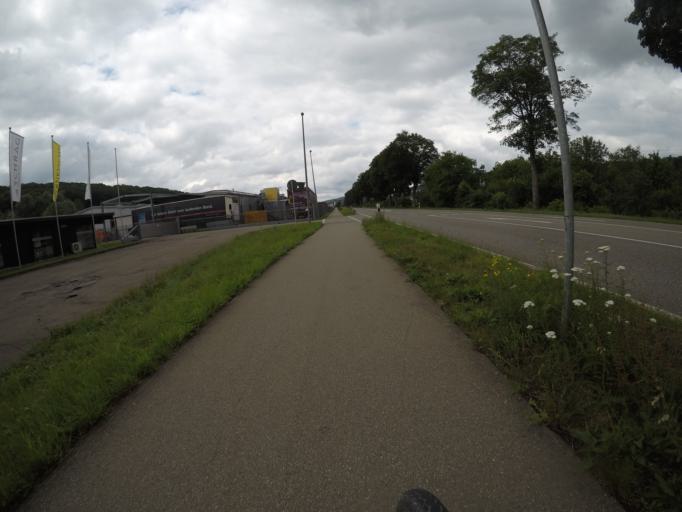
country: DE
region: Baden-Wuerttemberg
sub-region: Regierungsbezirk Stuttgart
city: Ebersbach an der Fils
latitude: 48.7175
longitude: 9.5520
